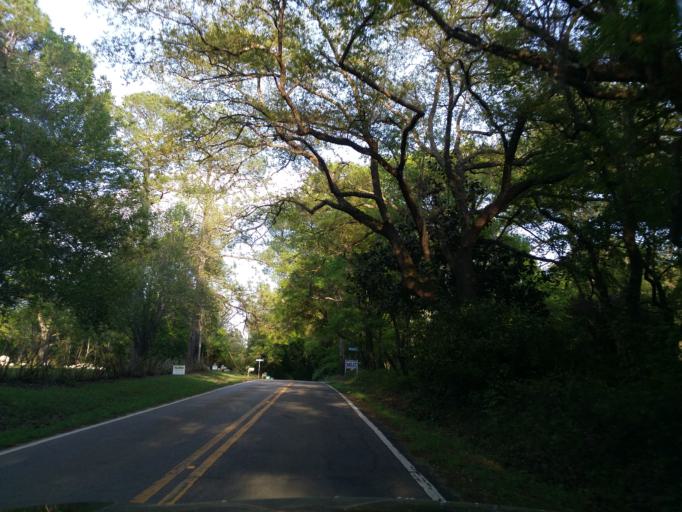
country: US
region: Florida
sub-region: Leon County
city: Tallahassee
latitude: 30.5216
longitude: -84.1150
